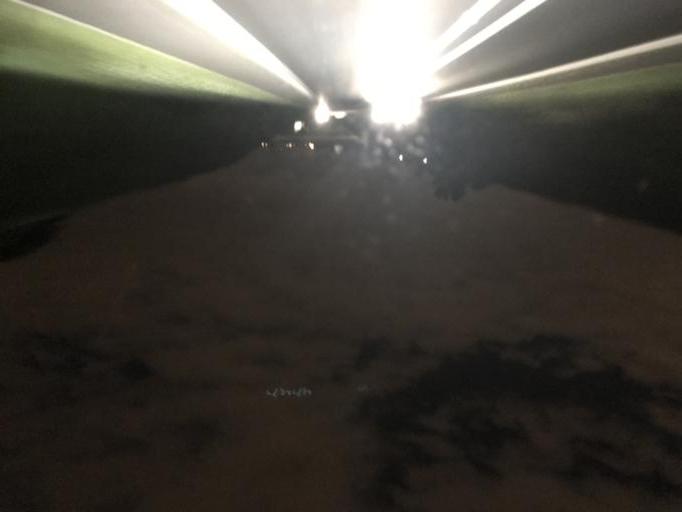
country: FR
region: Ile-de-France
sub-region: Departement des Yvelines
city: Sartrouville
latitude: 48.9354
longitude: 2.1725
